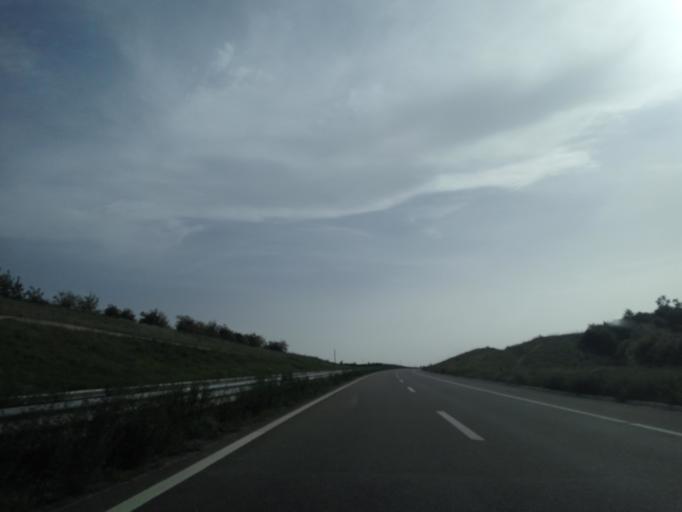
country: XK
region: Prizren
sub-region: Komuna e Therandes
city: Suva Reka
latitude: 42.3503
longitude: 20.7995
